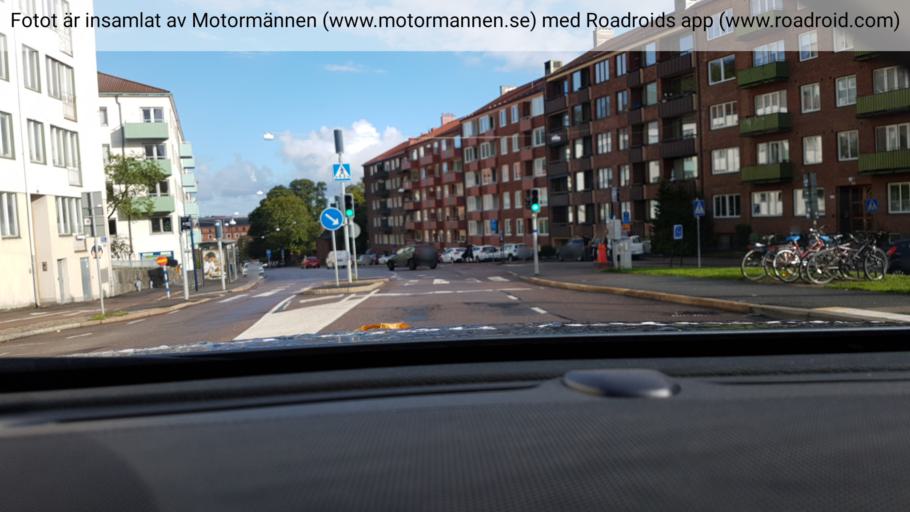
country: SE
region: Vaestra Goetaland
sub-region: Goteborg
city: Goeteborg
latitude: 57.6908
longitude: 11.9880
